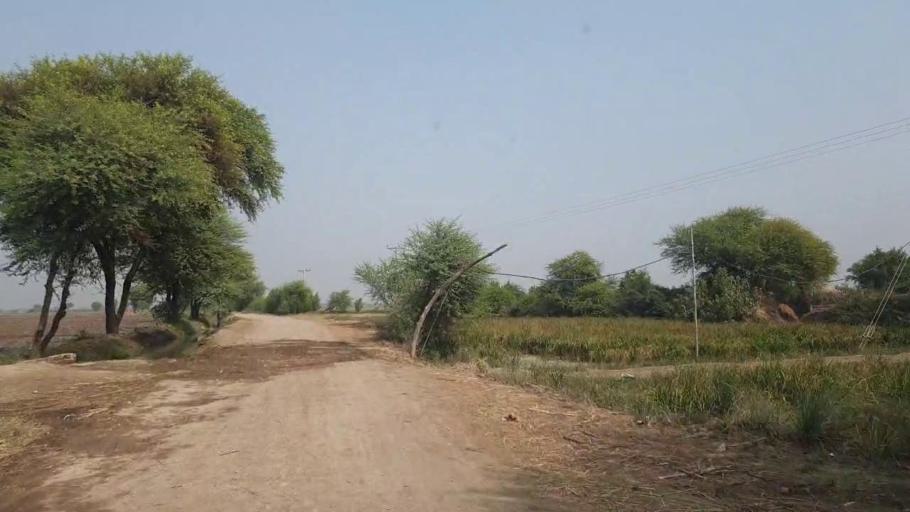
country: PK
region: Sindh
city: Matli
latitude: 25.1448
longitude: 68.7290
